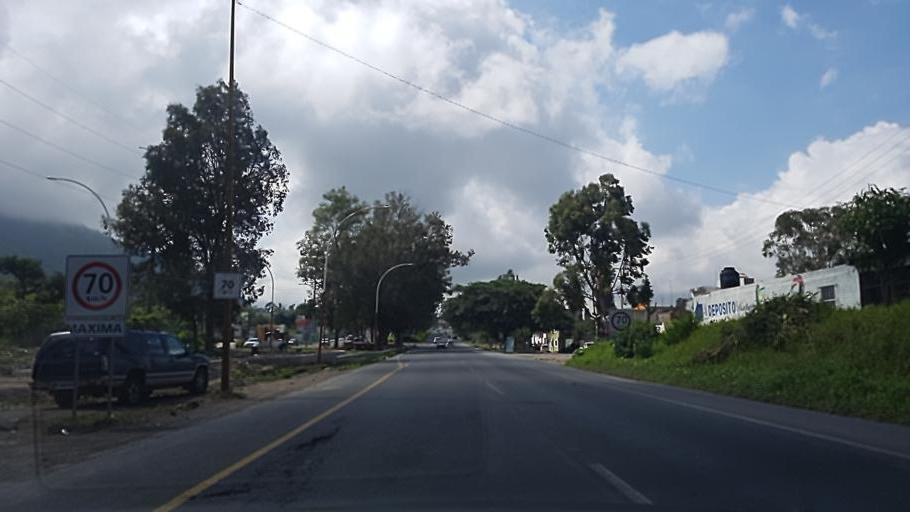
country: MX
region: Nayarit
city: Tepic
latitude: 21.4956
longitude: -104.9070
